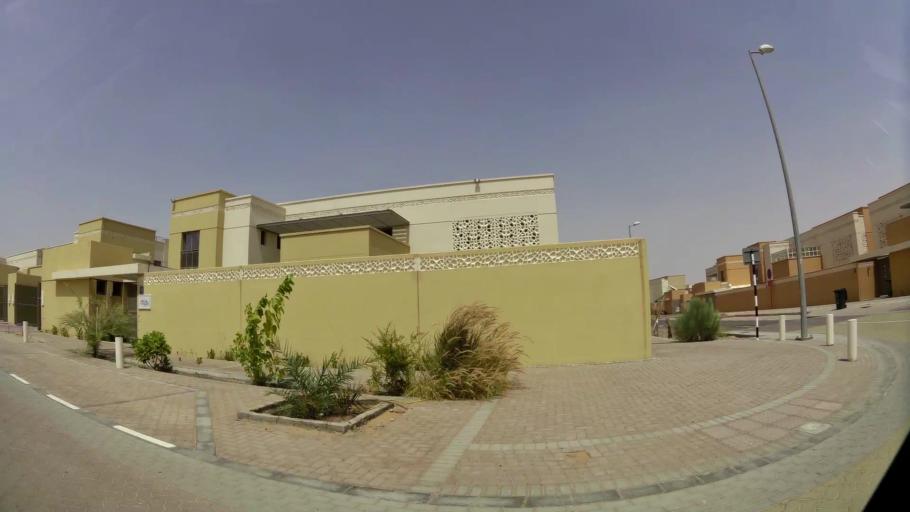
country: AE
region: Abu Dhabi
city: Al Ain
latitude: 24.1425
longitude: 55.6220
